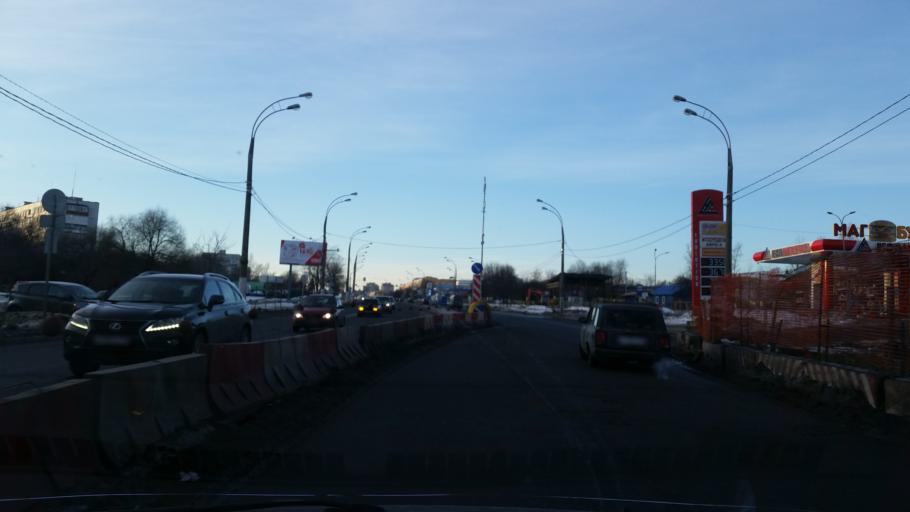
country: RU
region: Moskovskaya
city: Biryulevo Zapadnoye
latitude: 55.6076
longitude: 37.6226
